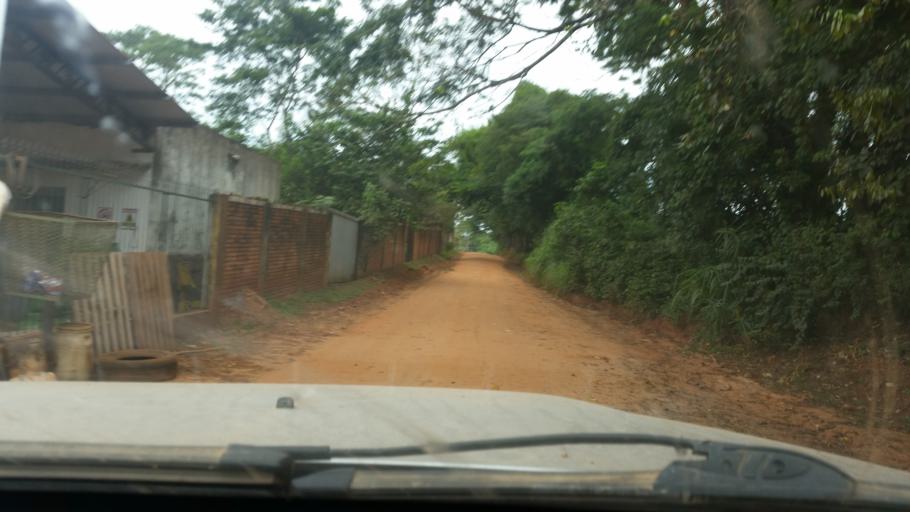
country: PY
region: Guaira
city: Independencia
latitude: -25.7033
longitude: -56.1917
